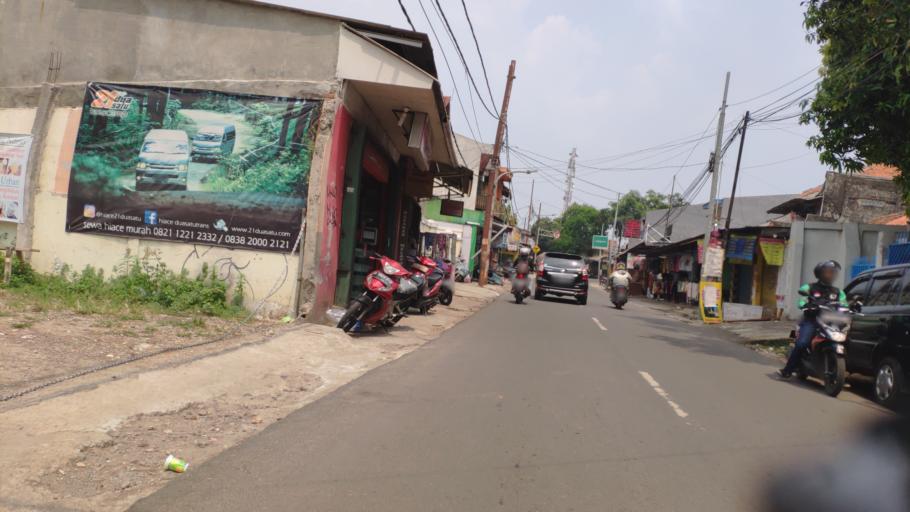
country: ID
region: West Java
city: Depok
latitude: -6.3450
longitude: 106.8316
